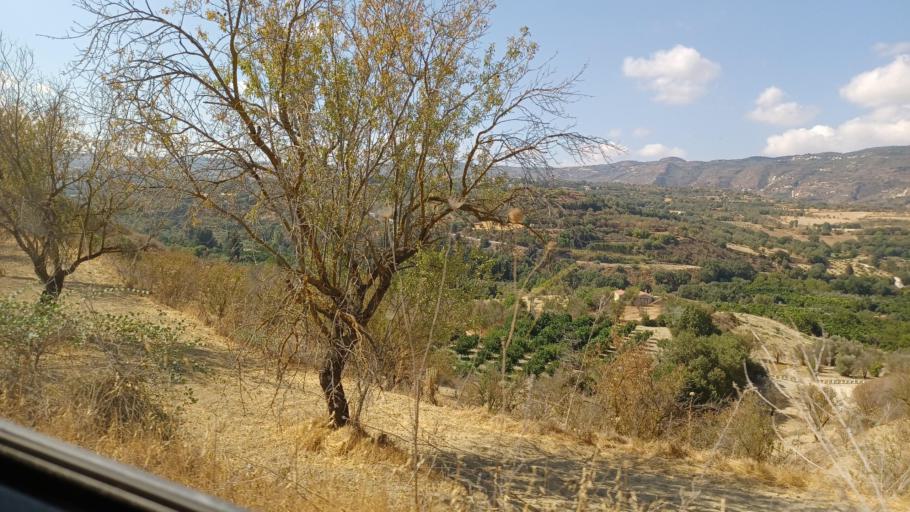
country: CY
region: Pafos
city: Tala
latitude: 34.9370
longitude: 32.4775
